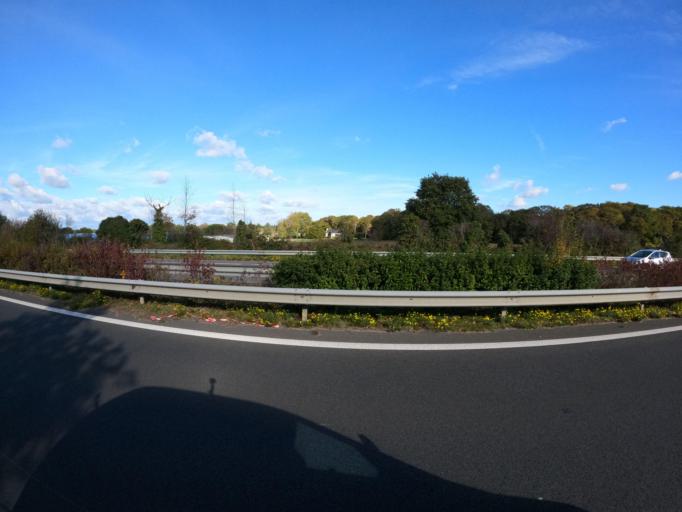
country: FR
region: Pays de la Loire
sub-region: Departement de la Loire-Atlantique
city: Pornichet
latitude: 47.2895
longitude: -2.3299
